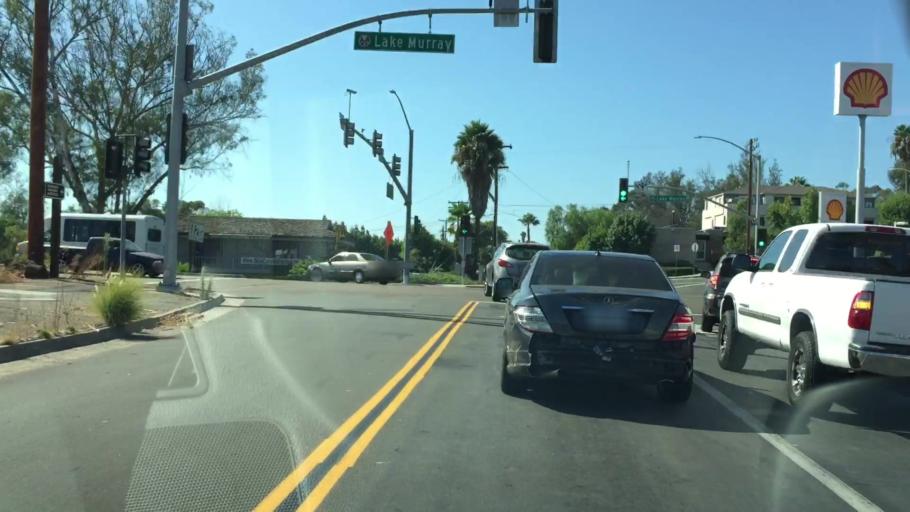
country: US
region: California
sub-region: San Diego County
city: La Mesa
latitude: 32.7749
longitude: -117.0451
